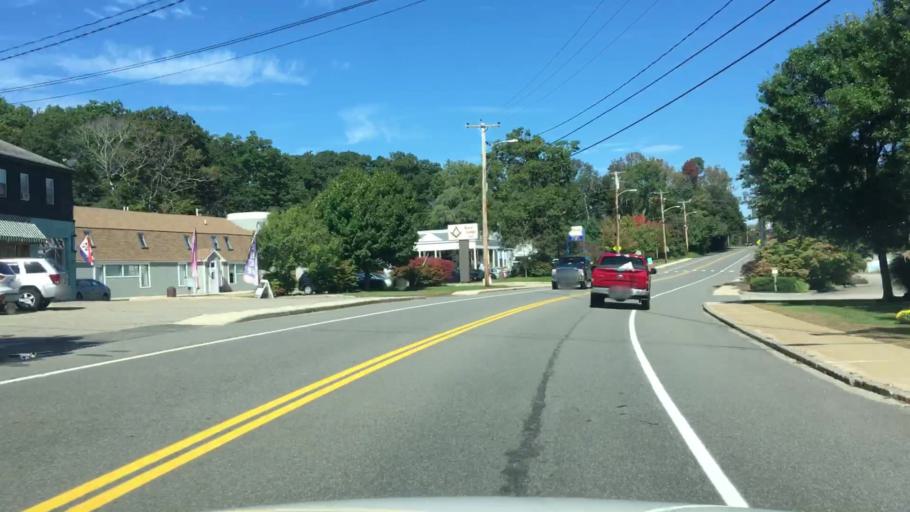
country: US
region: Maine
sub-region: York County
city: Kittery
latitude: 43.0894
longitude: -70.7367
